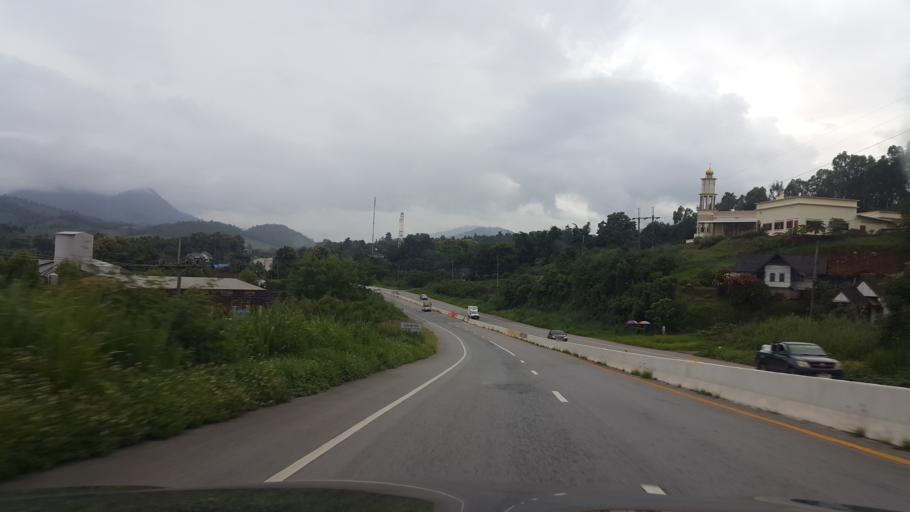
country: TH
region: Lampang
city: Wang Nuea
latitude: 19.1249
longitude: 99.4850
